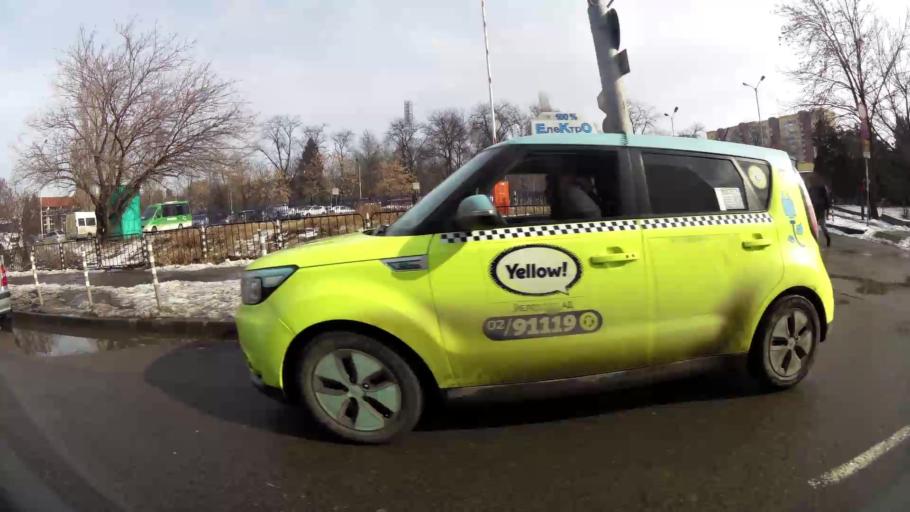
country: BG
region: Sofia-Capital
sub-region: Stolichna Obshtina
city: Sofia
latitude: 42.7035
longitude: 23.3595
